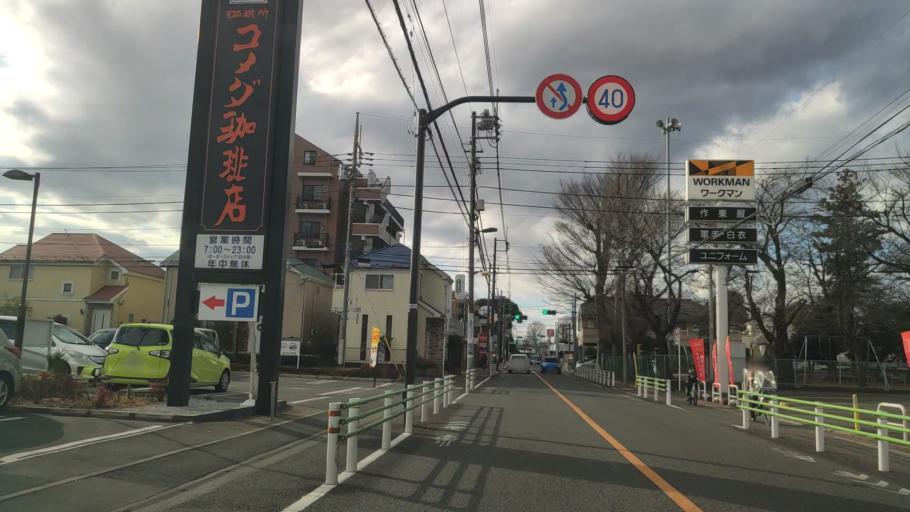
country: JP
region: Tokyo
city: Kokubunji
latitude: 35.7168
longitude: 139.4577
